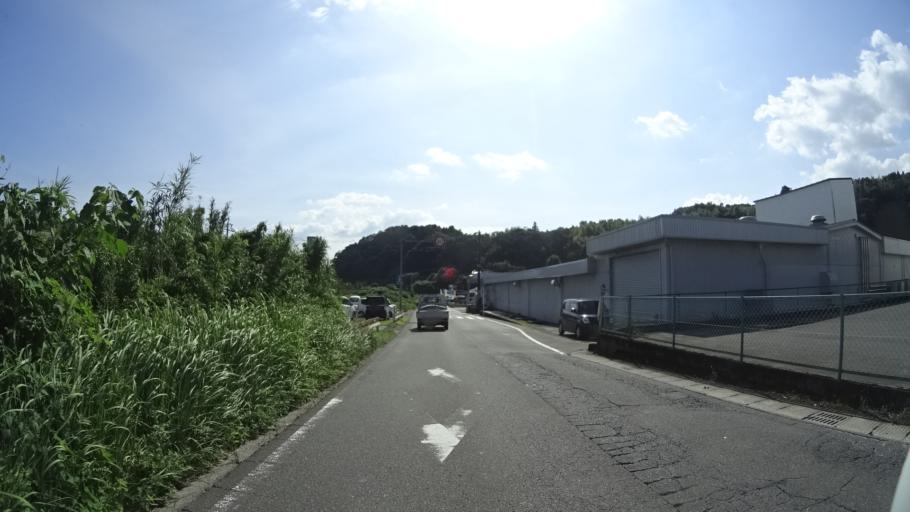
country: JP
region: Kagoshima
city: Kagoshima-shi
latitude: 31.6692
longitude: 130.5601
